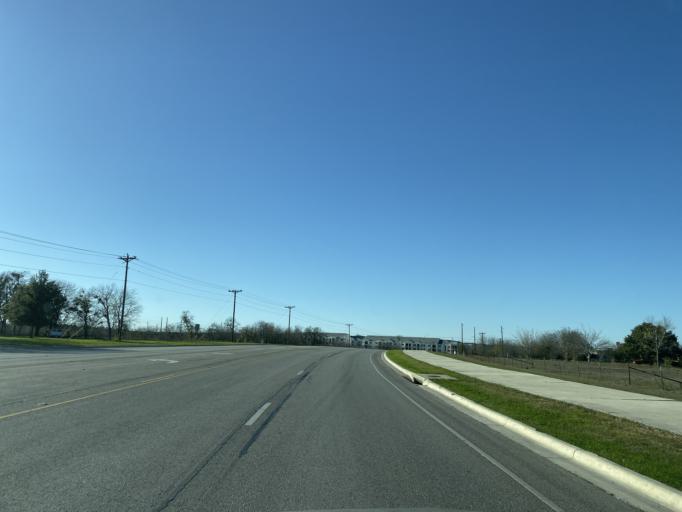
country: US
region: Texas
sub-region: Guadalupe County
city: Redwood
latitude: 29.8282
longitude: -97.9581
